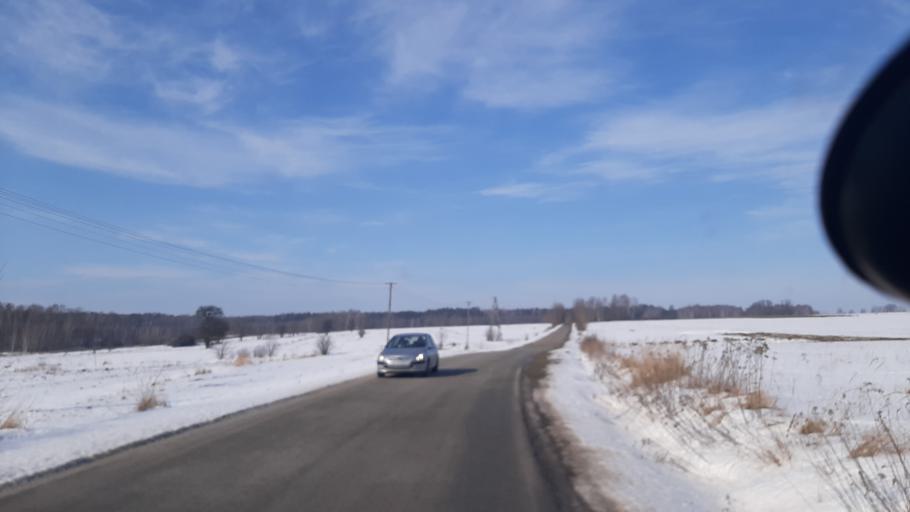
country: PL
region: Lublin Voivodeship
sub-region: Powiat pulawski
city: Kurow
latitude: 51.4543
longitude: 22.1843
